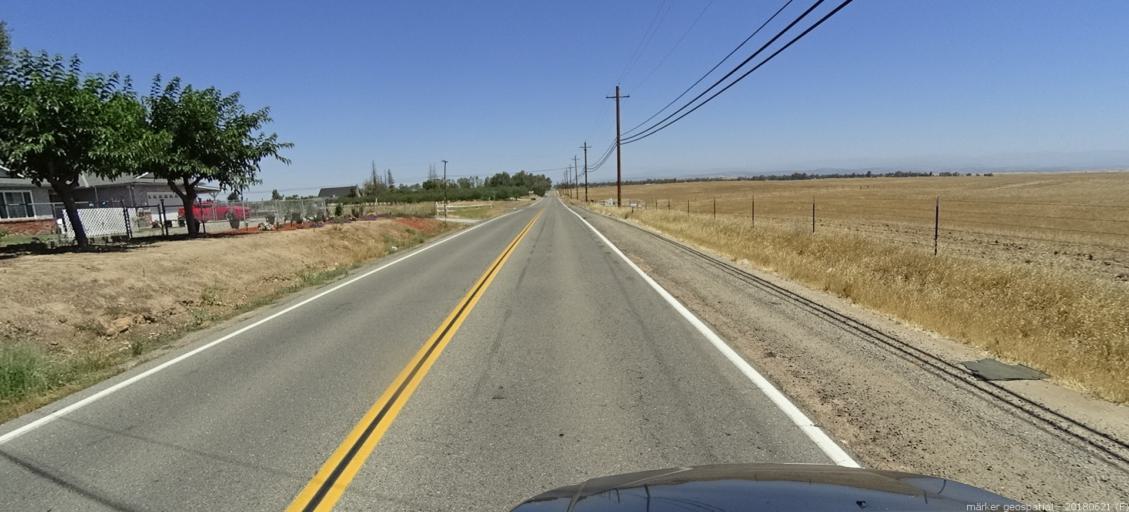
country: US
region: California
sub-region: Madera County
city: Bonadelle Ranchos-Madera Ranchos
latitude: 36.9511
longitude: -119.8940
